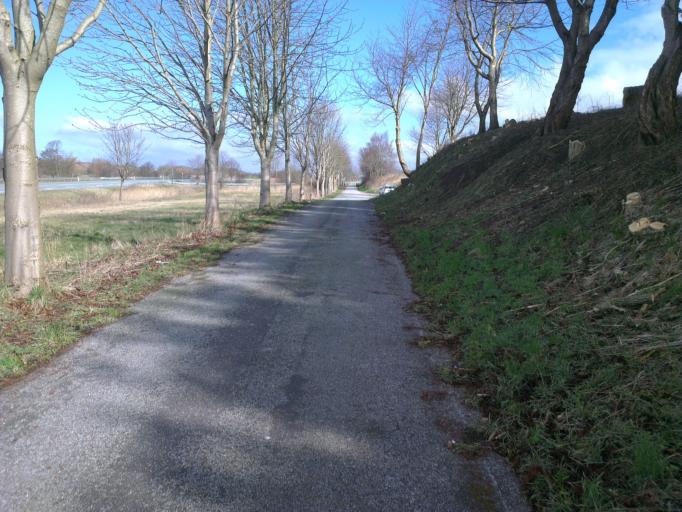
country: DK
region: Capital Region
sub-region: Frederikssund Kommune
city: Frederikssund
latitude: 55.8538
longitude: 12.0873
